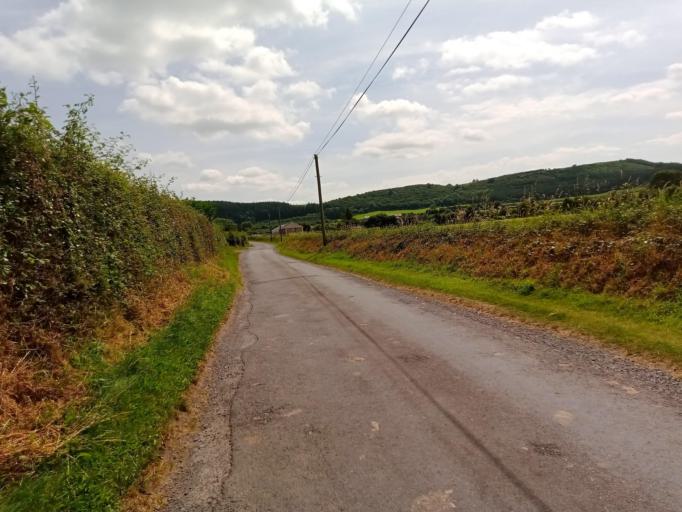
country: IE
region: Leinster
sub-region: Laois
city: Rathdowney
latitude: 52.8103
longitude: -7.4691
